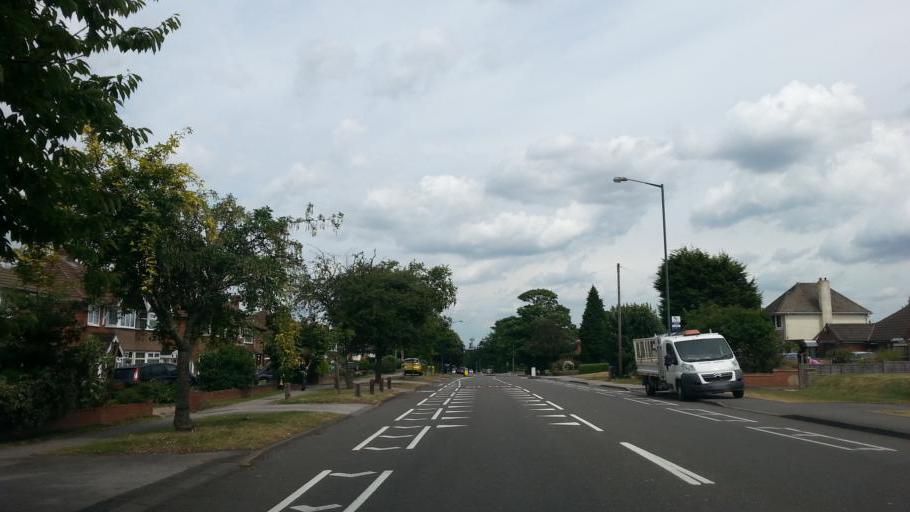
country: GB
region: England
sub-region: Solihull
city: Chelmsley Wood
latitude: 52.4842
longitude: -1.7561
